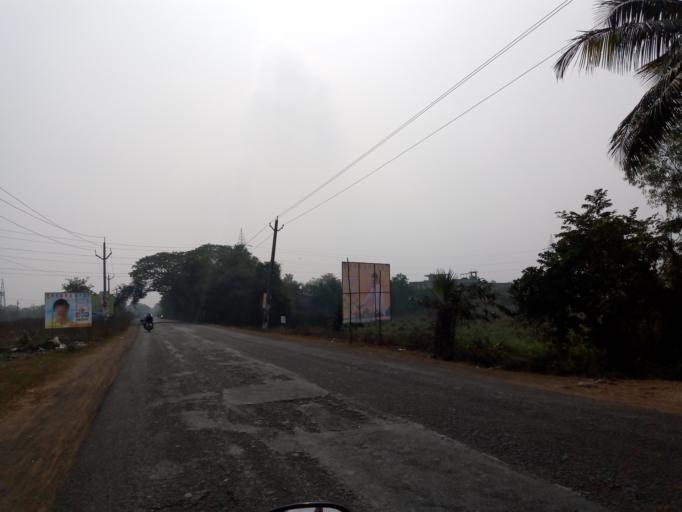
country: IN
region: Andhra Pradesh
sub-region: West Godavari
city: Bhimavaram
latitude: 16.5794
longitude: 81.4763
